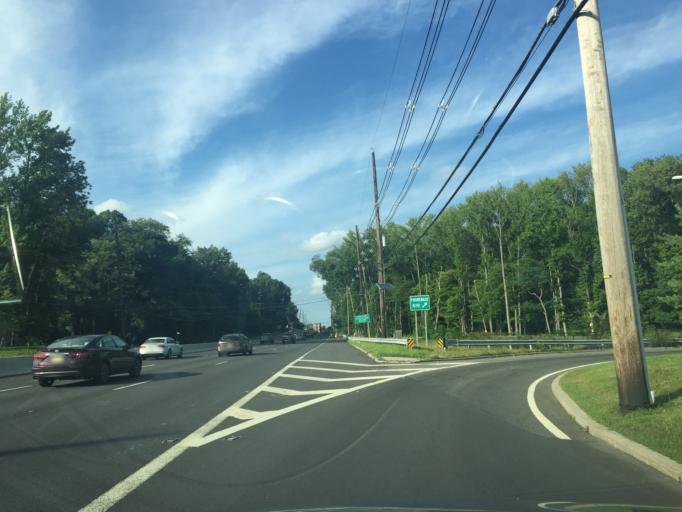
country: US
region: New Jersey
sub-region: Middlesex County
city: Heathcote
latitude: 40.3878
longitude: -74.5694
